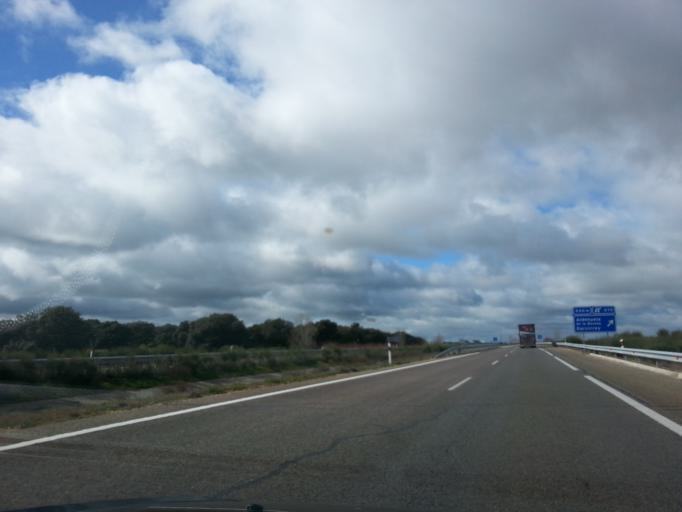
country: ES
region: Castille and Leon
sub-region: Provincia de Salamanca
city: Aldehuela de la Boveda
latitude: 40.8553
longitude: -6.0378
